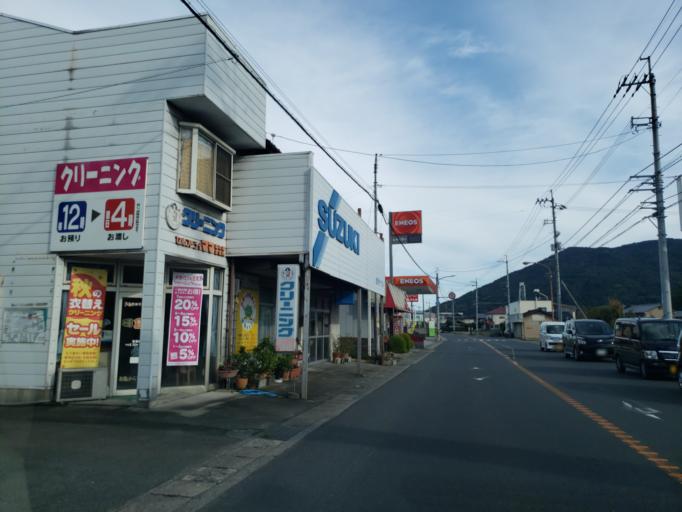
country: JP
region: Tokushima
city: Wakimachi
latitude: 34.0658
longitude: 134.1699
